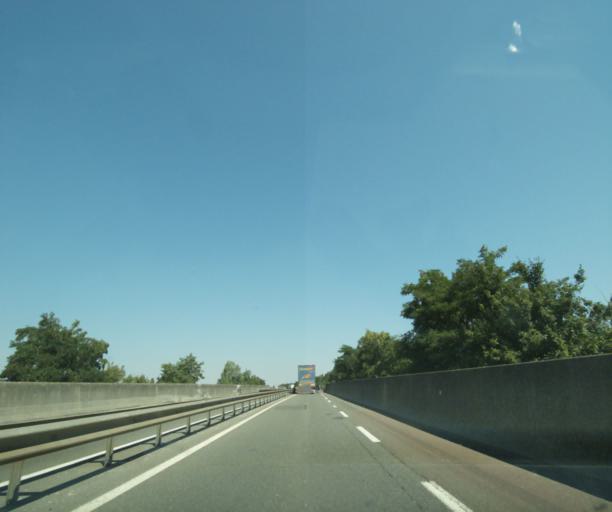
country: FR
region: Champagne-Ardenne
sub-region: Departement de la Haute-Marne
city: Saint-Dizier
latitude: 48.6351
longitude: 4.9231
